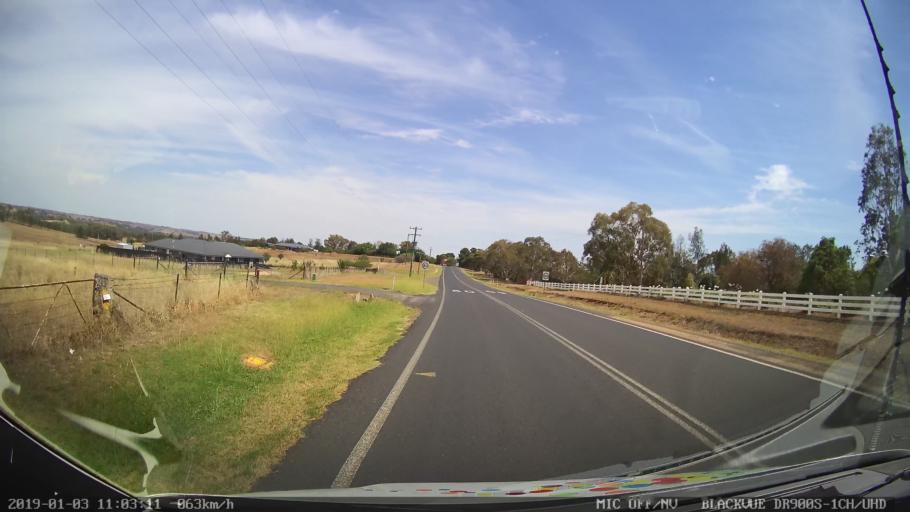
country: AU
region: New South Wales
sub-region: Young
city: Young
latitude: -34.2927
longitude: 148.2962
